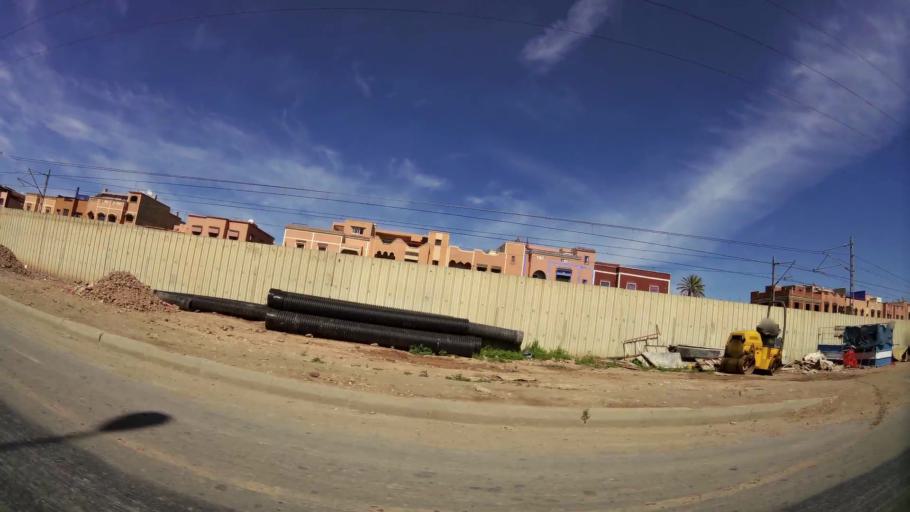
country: MA
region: Marrakech-Tensift-Al Haouz
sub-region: Marrakech
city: Marrakesh
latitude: 31.6366
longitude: -8.0385
